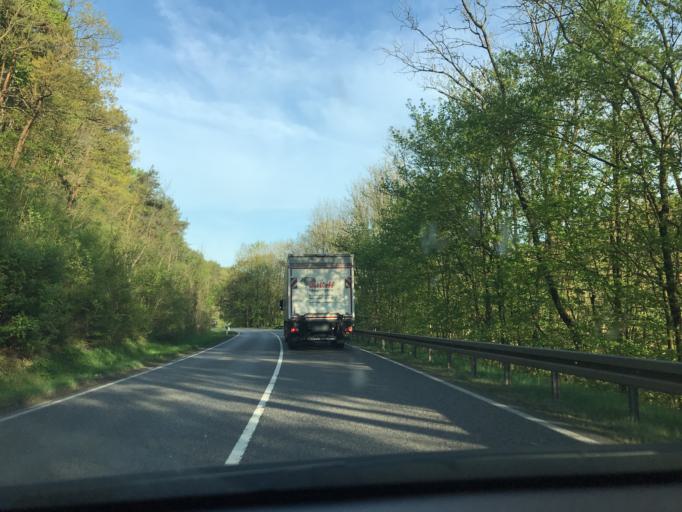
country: DE
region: Thuringia
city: Geisleden
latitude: 51.3602
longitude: 10.1734
